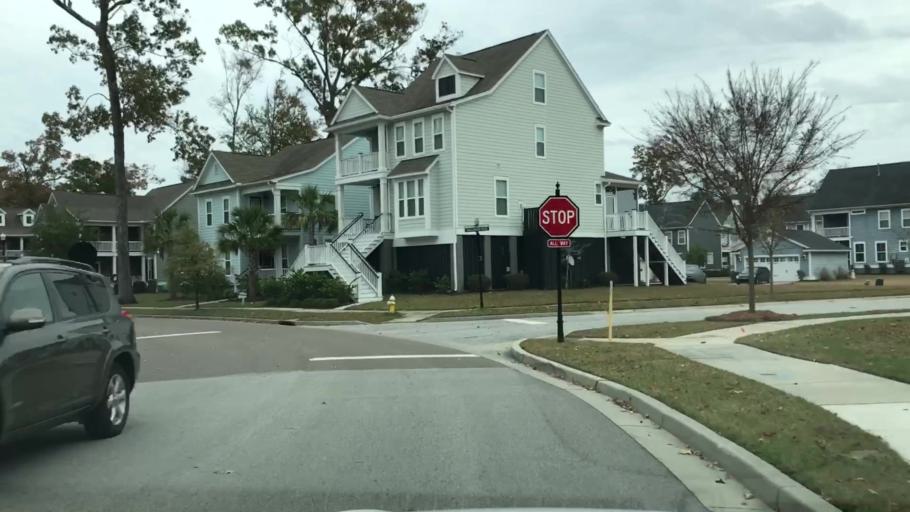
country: US
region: South Carolina
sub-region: Charleston County
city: Shell Point
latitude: 32.8058
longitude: -80.0580
